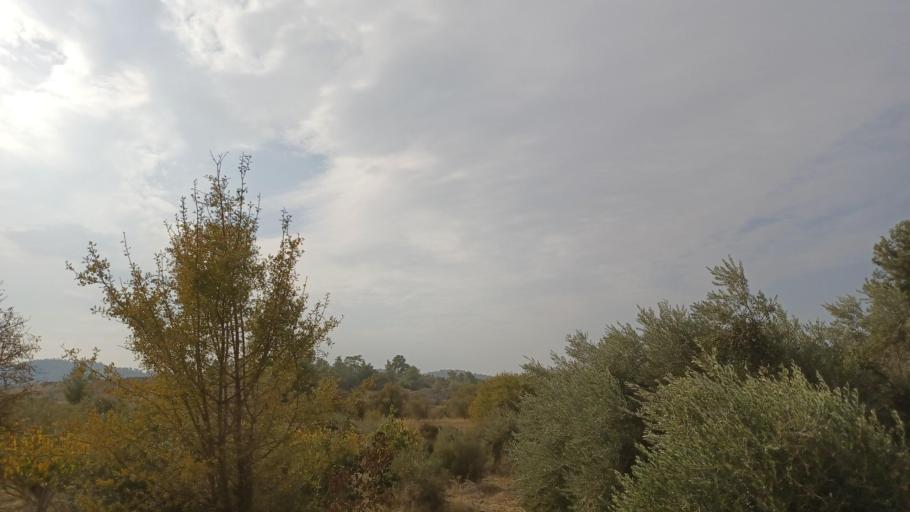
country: CY
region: Lefkosia
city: Klirou
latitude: 35.0342
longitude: 33.1355
